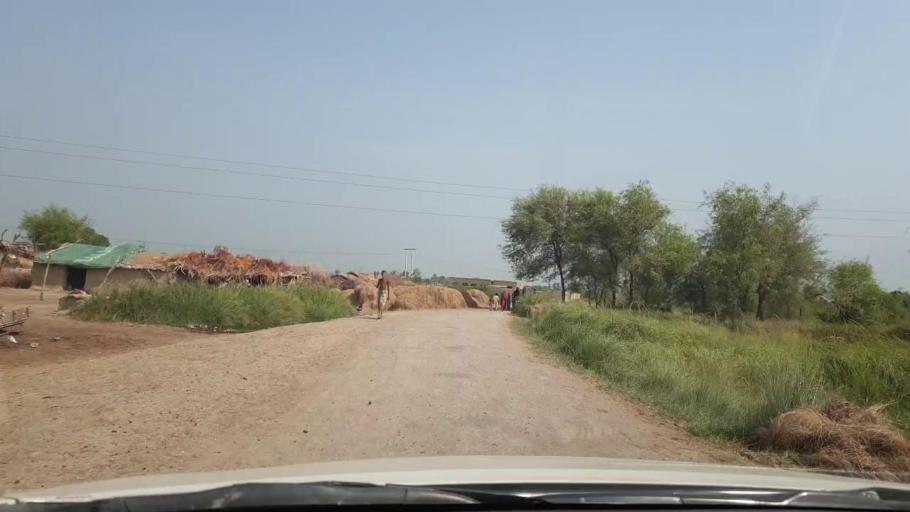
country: PK
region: Sindh
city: Shikarpur
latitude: 27.9727
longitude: 68.6705
